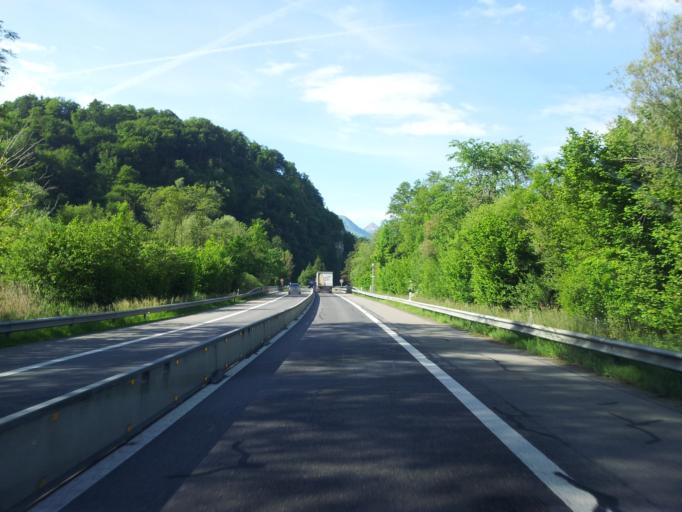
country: CH
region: Obwalden
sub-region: Obwalden
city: Kerns
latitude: 46.9162
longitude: 8.2674
